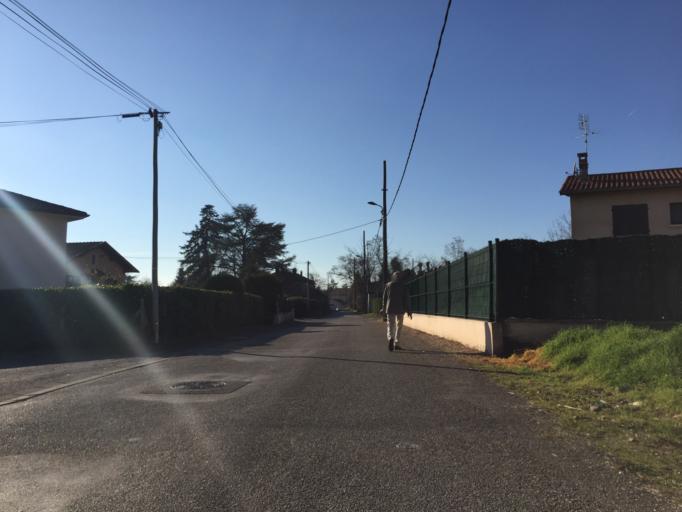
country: FR
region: Rhone-Alpes
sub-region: Departement de l'Ain
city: Saint-Maurice-de-Beynost
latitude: 45.8332
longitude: 4.9820
